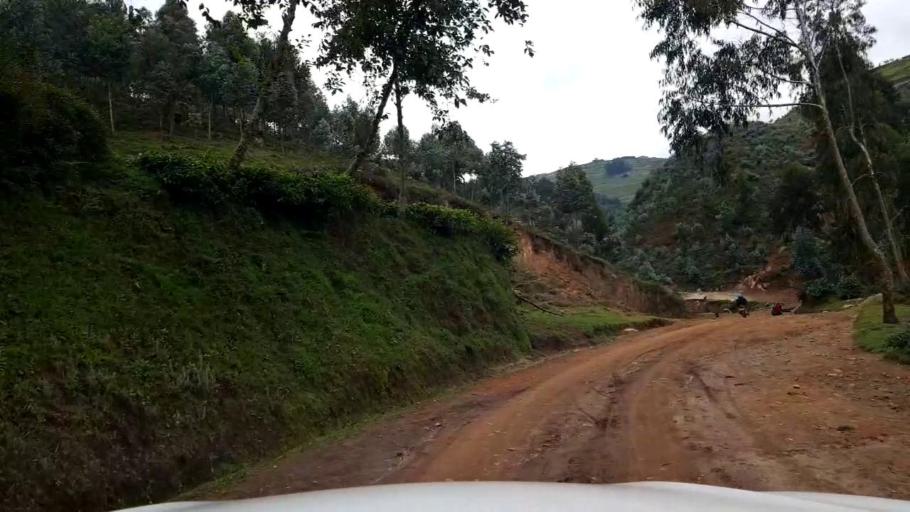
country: RW
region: Western Province
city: Kibuye
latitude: -1.9529
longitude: 29.4220
